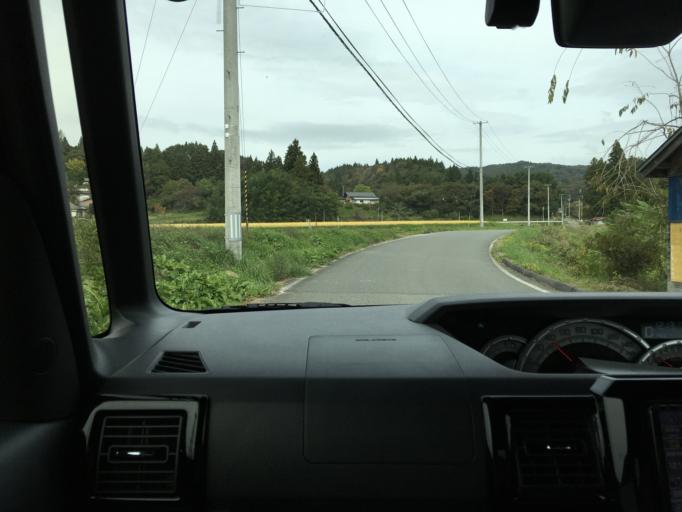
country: JP
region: Iwate
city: Ichinoseki
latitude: 39.0182
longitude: 141.3476
